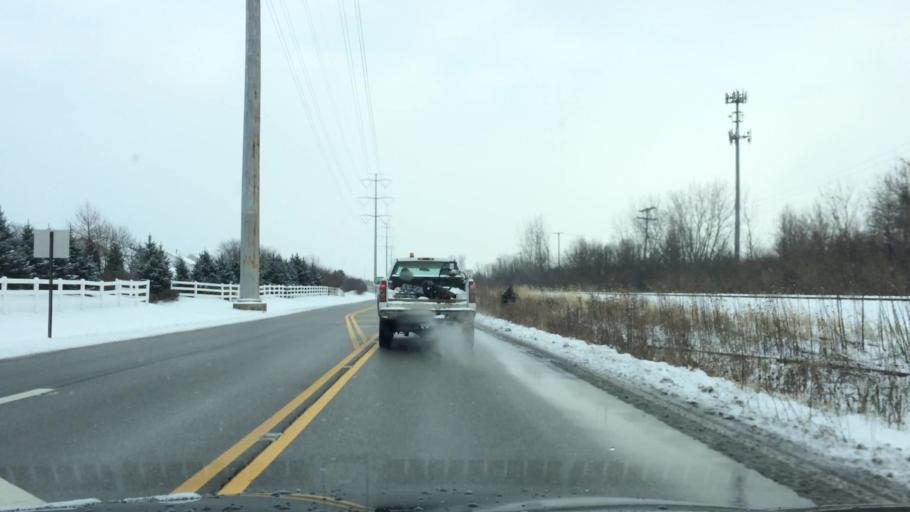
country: US
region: Ohio
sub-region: Franklin County
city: Hilliard
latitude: 40.0181
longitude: -83.1352
